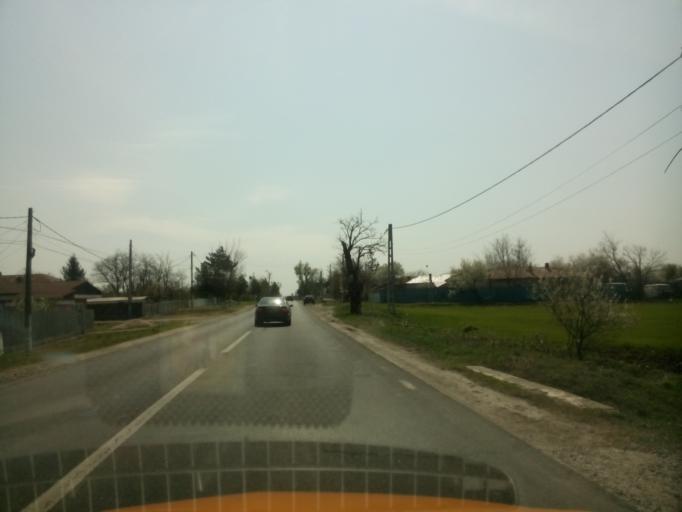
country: RO
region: Calarasi
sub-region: Comuna Frumusani
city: Frumusani
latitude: 44.2962
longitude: 26.3125
